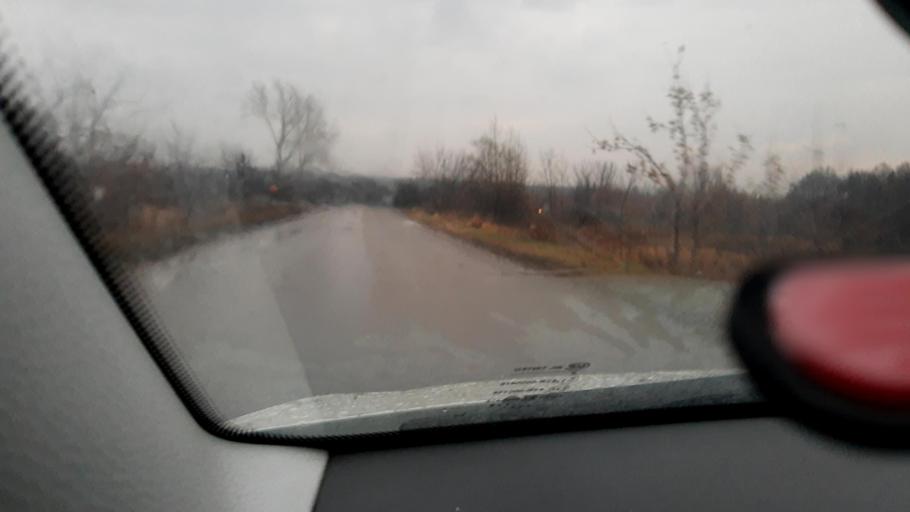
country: RU
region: Bashkortostan
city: Ufa
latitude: 54.8712
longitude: 56.1321
